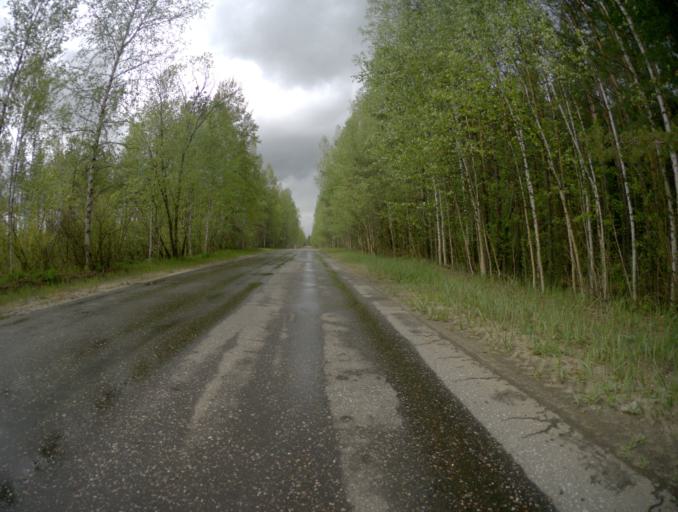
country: RU
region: Vladimir
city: Zolotkovo
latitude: 55.3531
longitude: 40.9153
